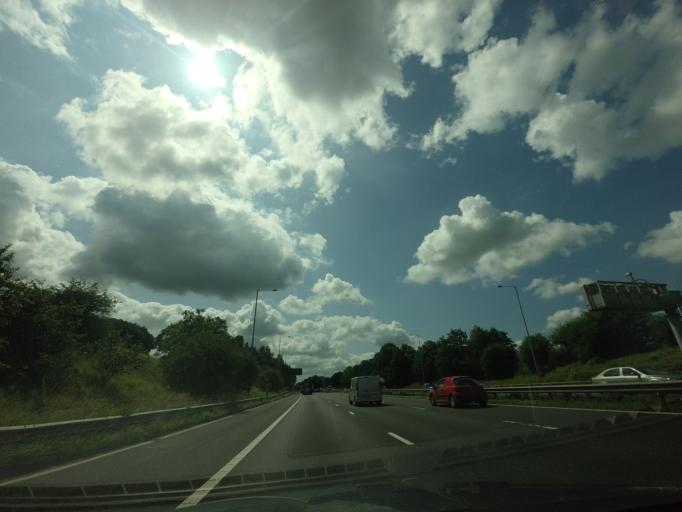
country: GB
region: England
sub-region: Lancashire
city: Euxton
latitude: 53.6637
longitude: -2.6901
